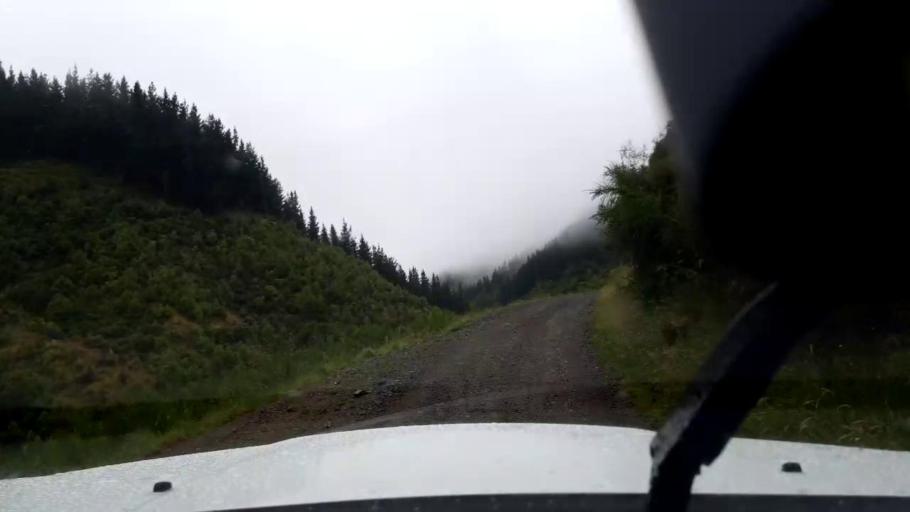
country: NZ
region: Canterbury
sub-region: Timaru District
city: Pleasant Point
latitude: -44.0438
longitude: 171.0190
